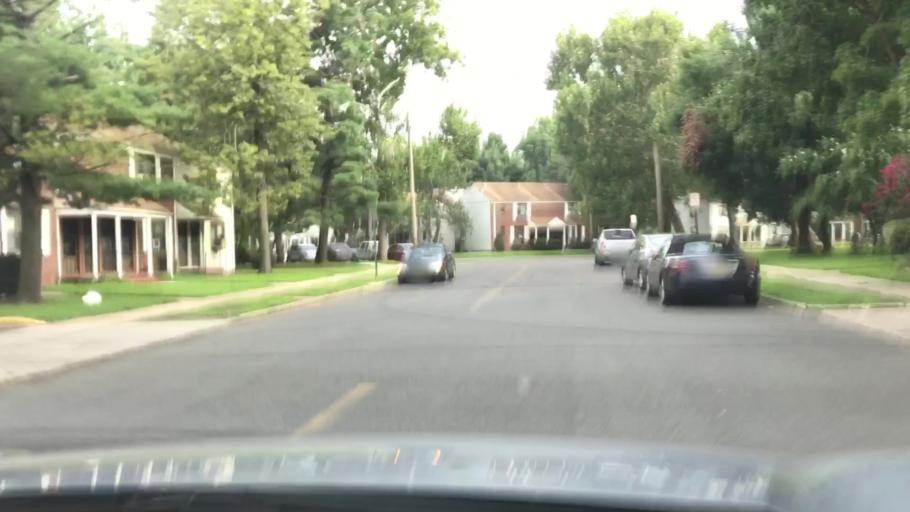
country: US
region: New Jersey
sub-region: Bergen County
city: New Milford
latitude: 40.9266
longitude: -74.0196
